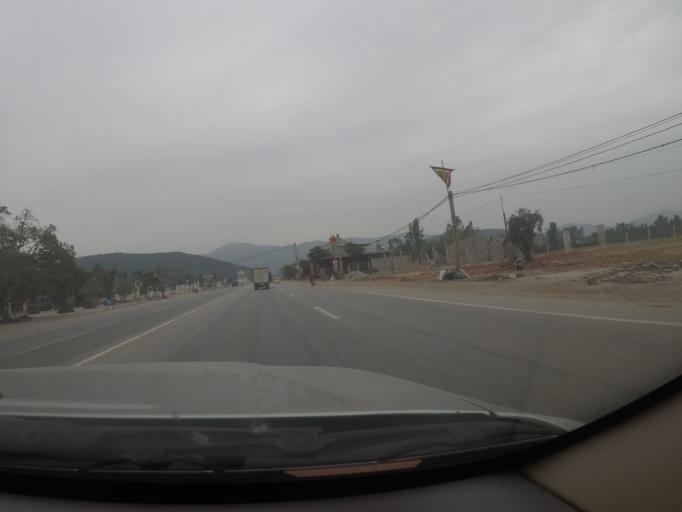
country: VN
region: Nghe An
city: Dien Chau
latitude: 18.9047
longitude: 105.6044
